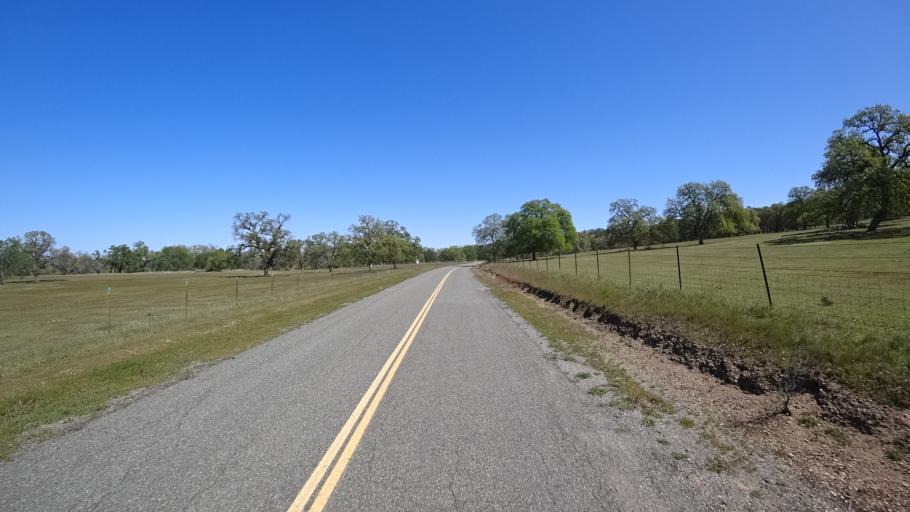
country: US
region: California
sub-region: Glenn County
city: Orland
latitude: 39.7343
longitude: -122.3995
